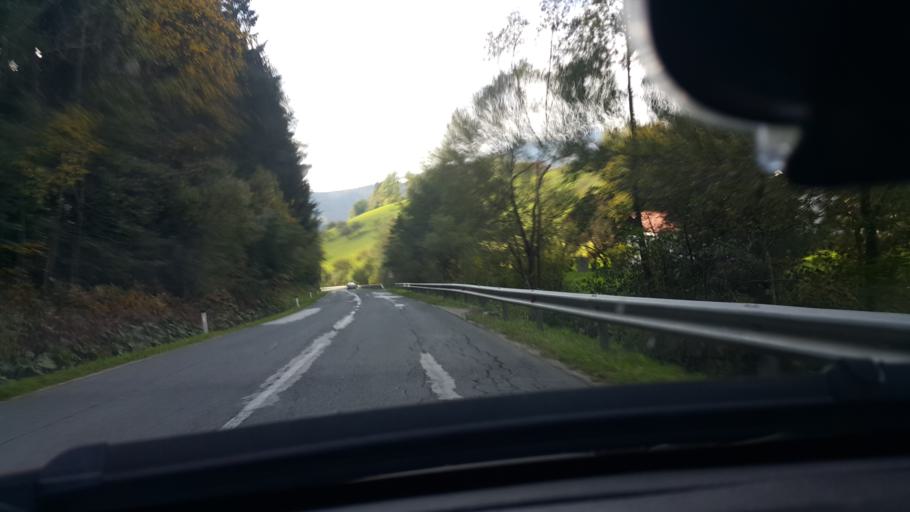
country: SI
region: Vitanje
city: Vitanje
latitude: 46.3860
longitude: 15.3118
